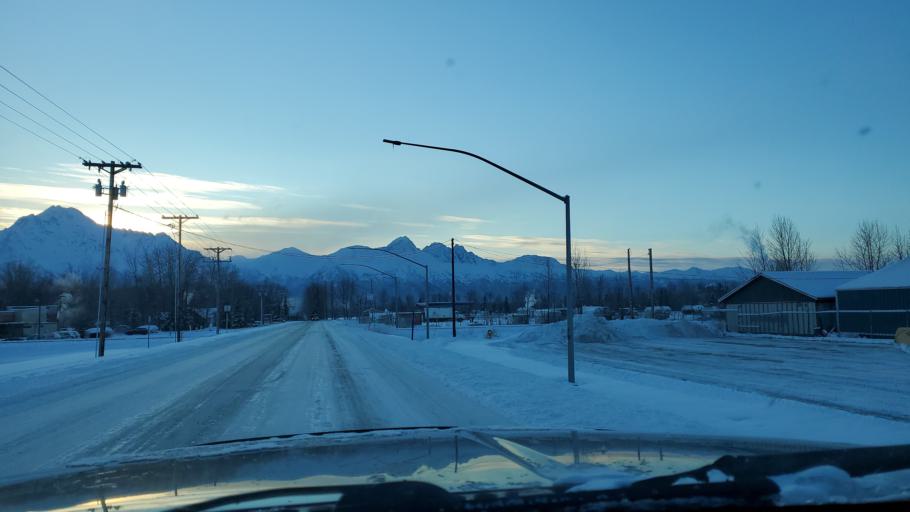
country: US
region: Alaska
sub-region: Matanuska-Susitna Borough
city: Palmer
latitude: 61.5875
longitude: -149.1106
